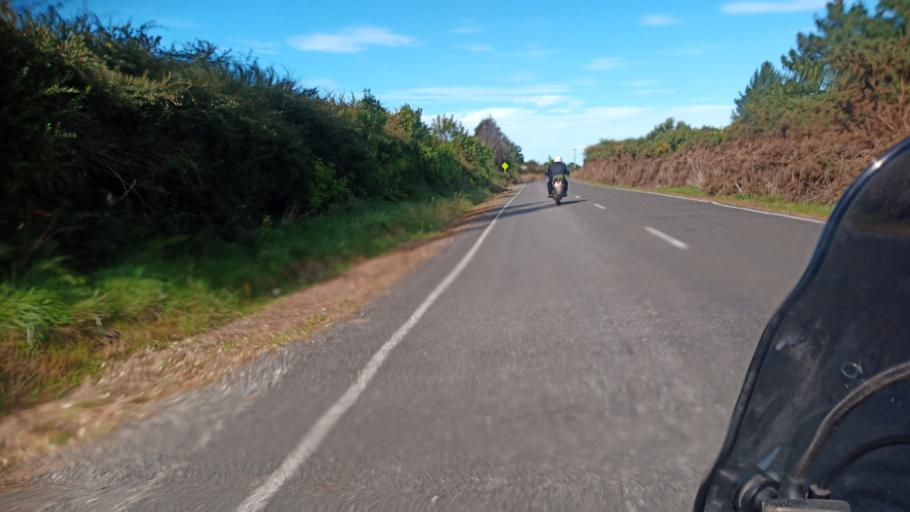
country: NZ
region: Hawke's Bay
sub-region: Wairoa District
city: Wairoa
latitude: -39.0607
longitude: 177.1264
